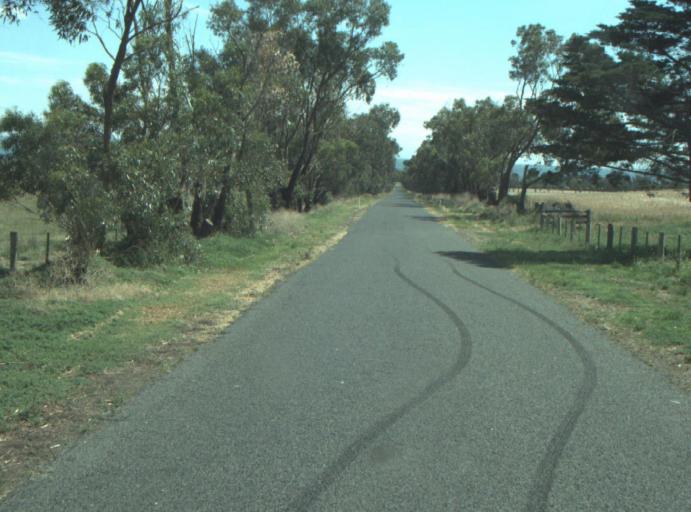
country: AU
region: Victoria
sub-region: Greater Geelong
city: Leopold
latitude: -38.1748
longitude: 144.4711
